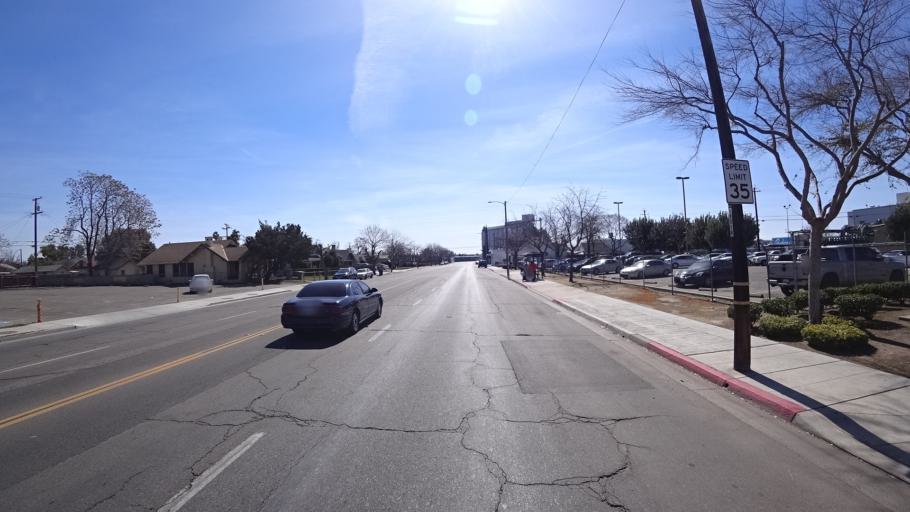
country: US
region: California
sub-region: Fresno County
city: Fresno
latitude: 36.7498
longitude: -119.8084
